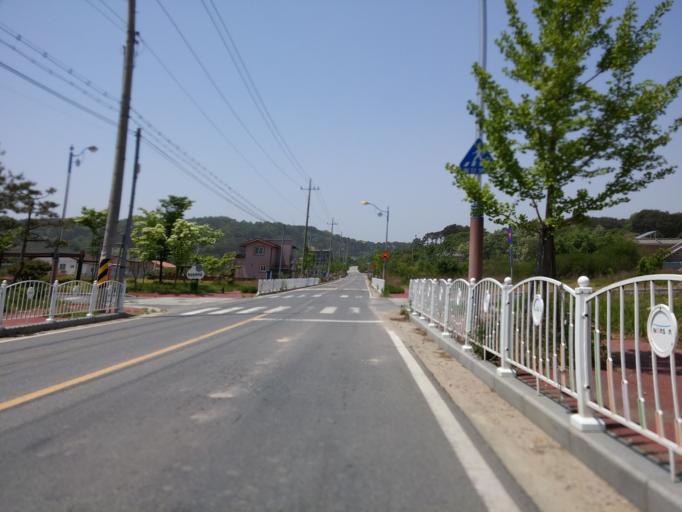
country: KR
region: Chungcheongnam-do
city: Nonsan
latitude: 36.2130
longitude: 127.1860
